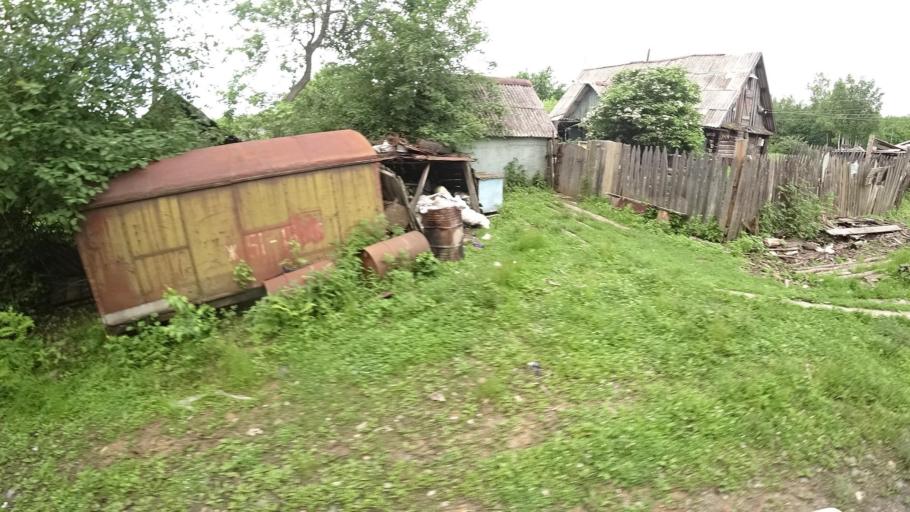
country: RU
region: Khabarovsk Krai
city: Amursk
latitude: 49.9065
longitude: 136.1329
